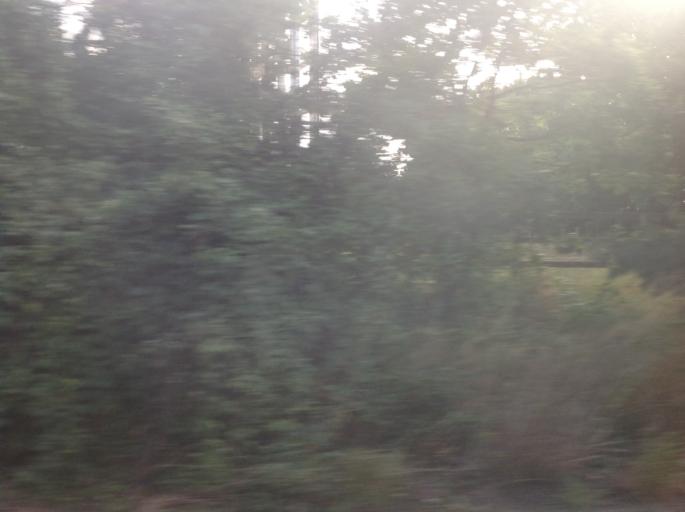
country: GB
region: England
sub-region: Suffolk
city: Felixstowe
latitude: 51.9793
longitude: 1.3296
